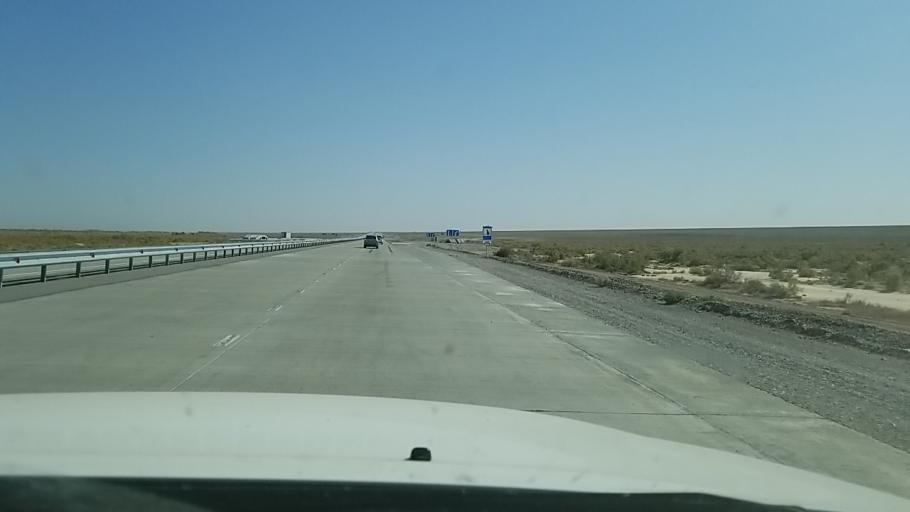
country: KZ
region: Almaty Oblysy
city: Kegen
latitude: 43.7561
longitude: 78.9342
